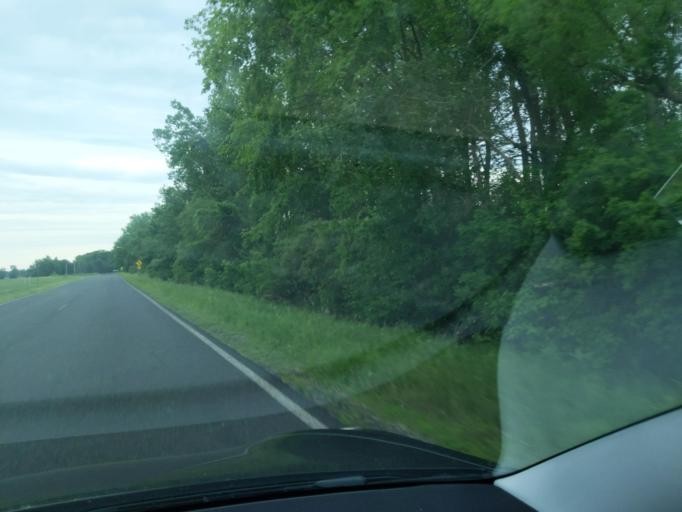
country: US
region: Michigan
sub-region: Isabella County
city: Mount Pleasant
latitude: 43.6188
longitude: -84.7347
